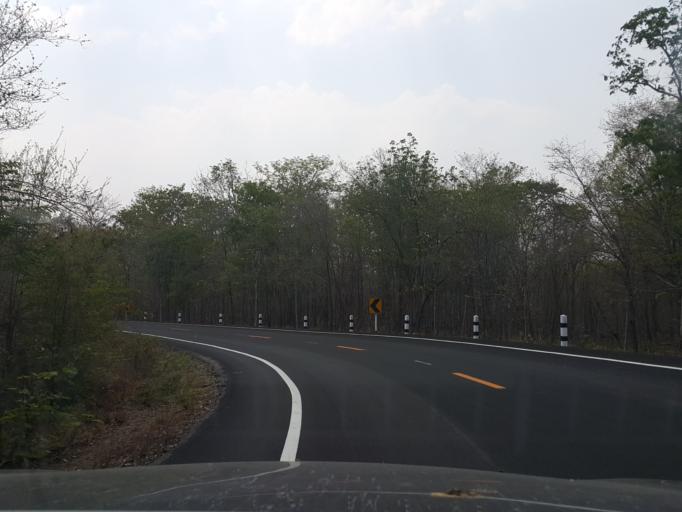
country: TH
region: Lampang
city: Mae Phrik
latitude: 17.4883
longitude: 99.1048
